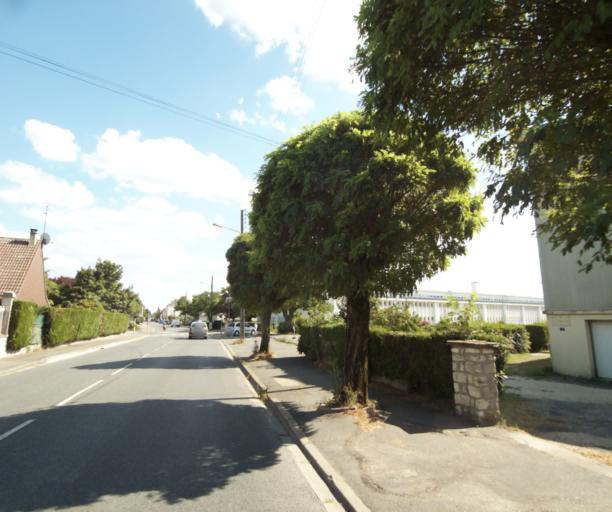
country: FR
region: Centre
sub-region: Departement du Loiret
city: La Chapelle-Saint-Mesmin
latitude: 47.8926
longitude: 1.8396
